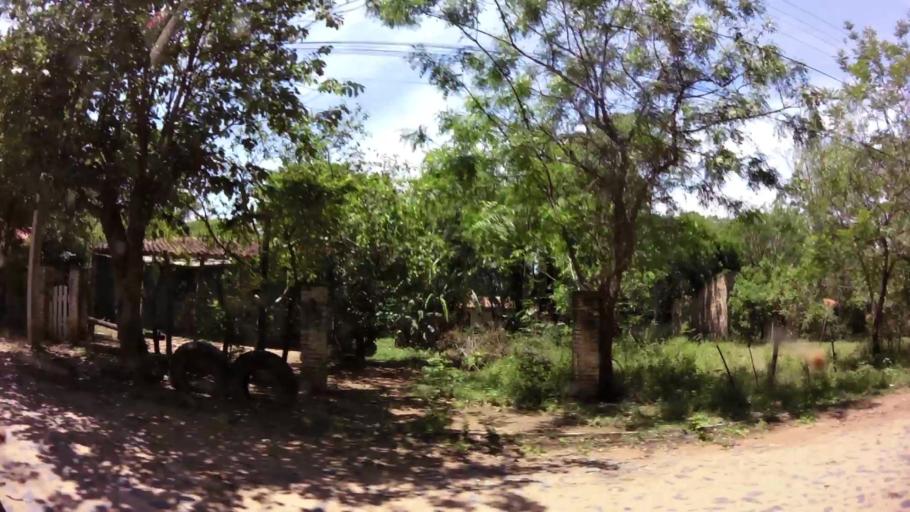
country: PY
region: Central
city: Colonia Mariano Roque Alonso
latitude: -25.2002
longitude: -57.5509
